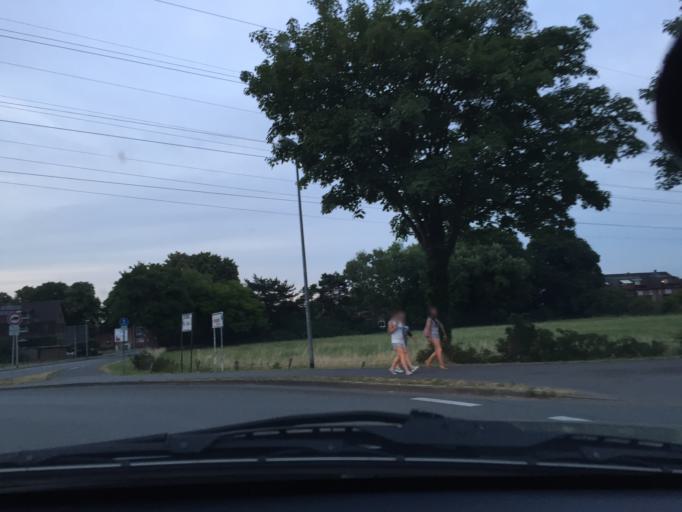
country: DE
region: North Rhine-Westphalia
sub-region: Regierungsbezirk Dusseldorf
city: Kleve
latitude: 51.7906
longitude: 6.1548
